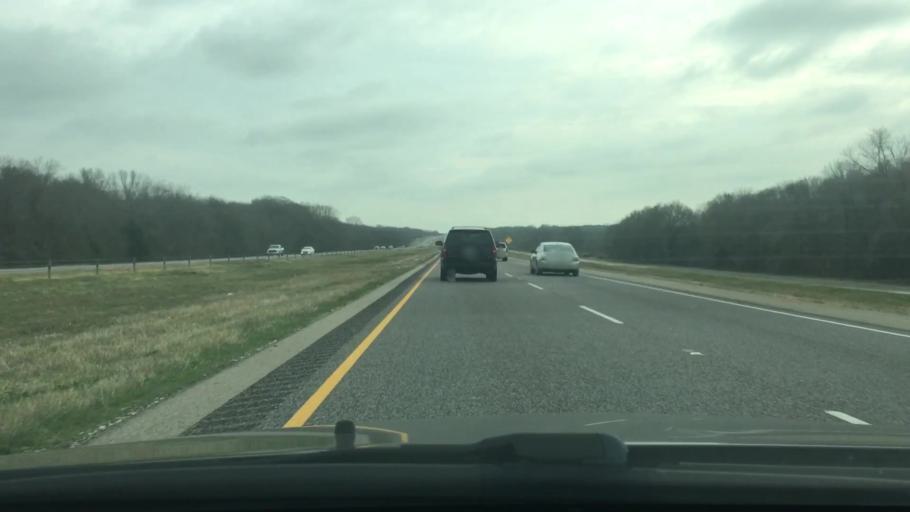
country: US
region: Texas
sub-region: Freestone County
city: Fairfield
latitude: 31.6551
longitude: -96.1609
